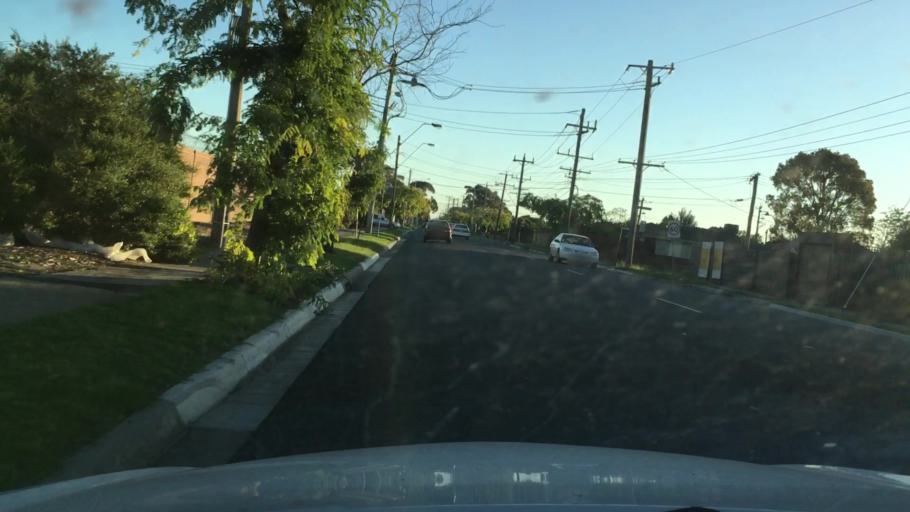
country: AU
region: Victoria
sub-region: Greater Dandenong
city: Noble Park
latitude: -37.9780
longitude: 145.1659
